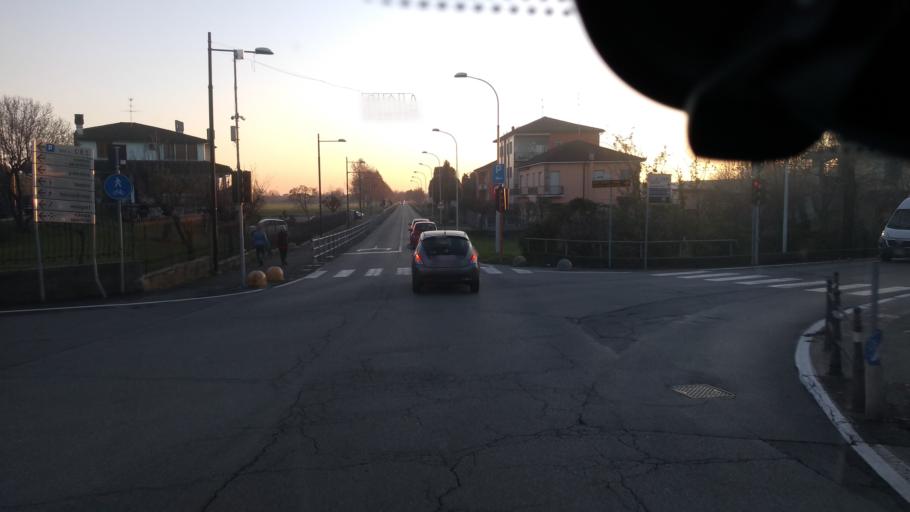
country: IT
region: Lombardy
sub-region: Provincia di Bergamo
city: Casirate d'Adda
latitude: 45.4916
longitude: 9.5671
